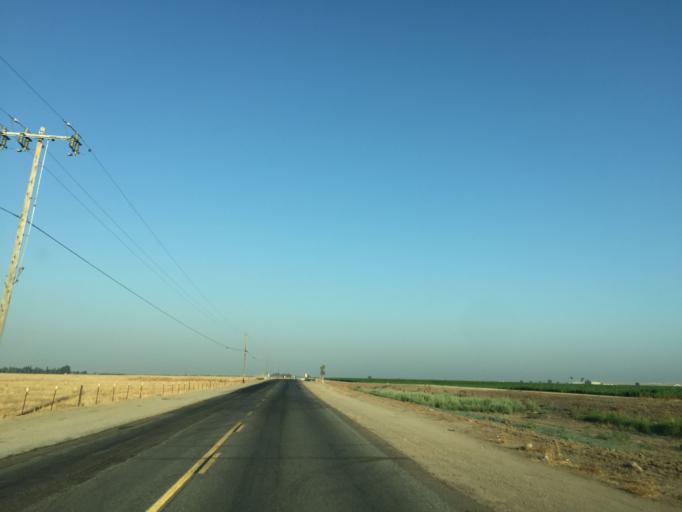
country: US
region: California
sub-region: Tulare County
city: Cutler
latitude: 36.4580
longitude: -119.3327
